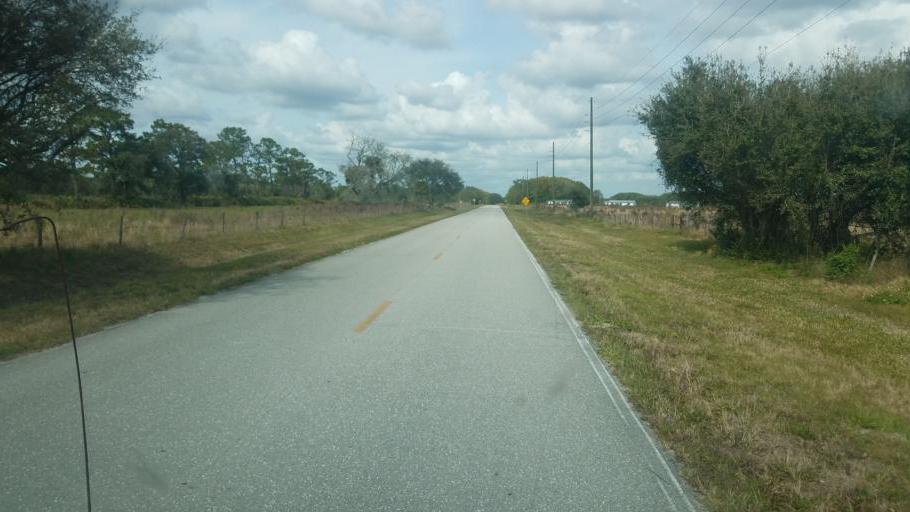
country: US
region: Florida
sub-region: Okeechobee County
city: Cypress Quarters
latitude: 27.5131
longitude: -80.7767
